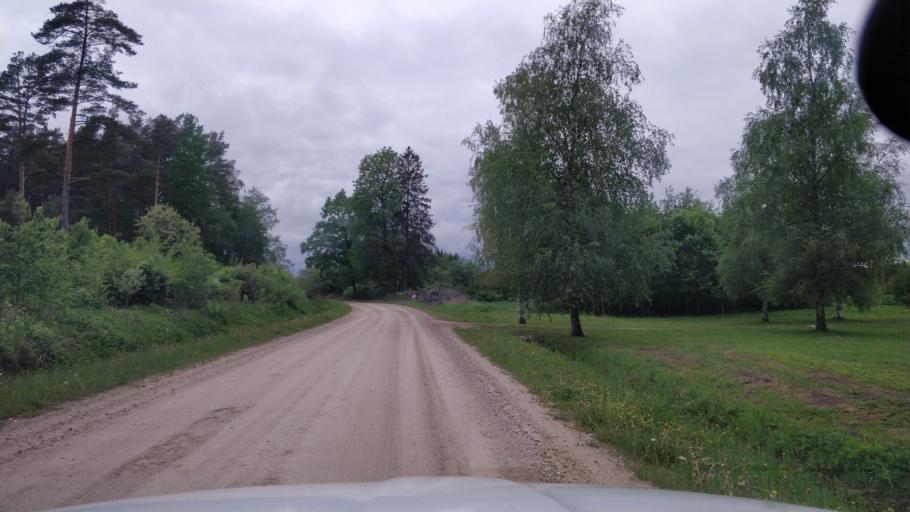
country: EE
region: Paernumaa
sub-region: Halinga vald
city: Parnu-Jaagupi
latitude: 58.7099
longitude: 24.3490
